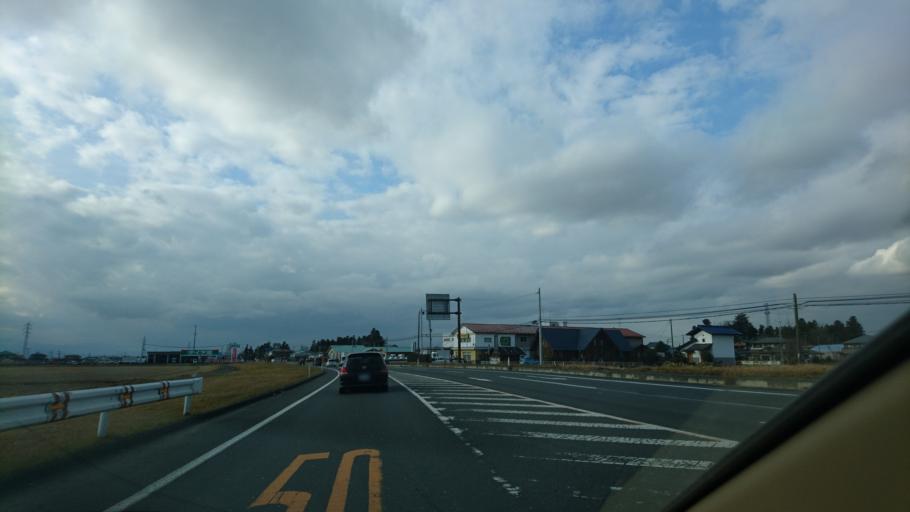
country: JP
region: Miyagi
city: Kogota
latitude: 38.5595
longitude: 141.0339
